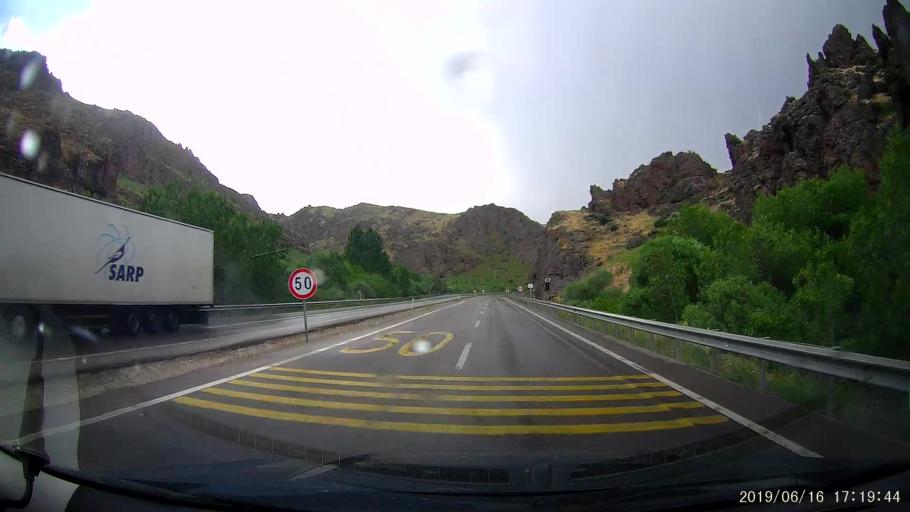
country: TR
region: Erzincan
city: Tercan
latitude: 39.8009
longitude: 40.5245
